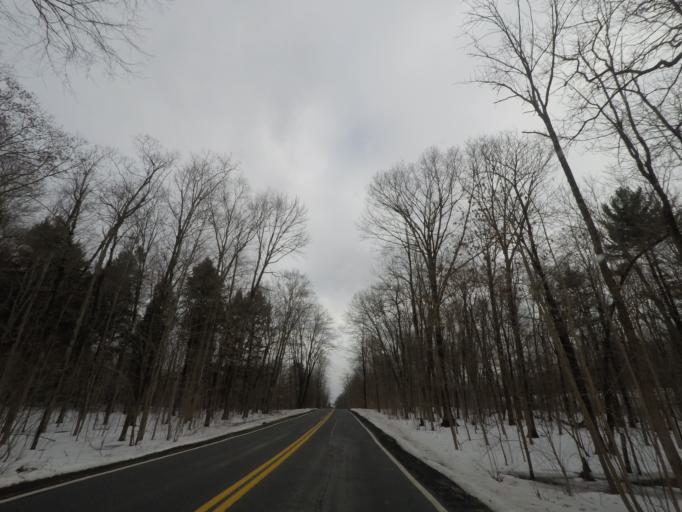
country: US
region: New York
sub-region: Schenectady County
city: Rotterdam
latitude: 42.7358
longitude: -73.9632
